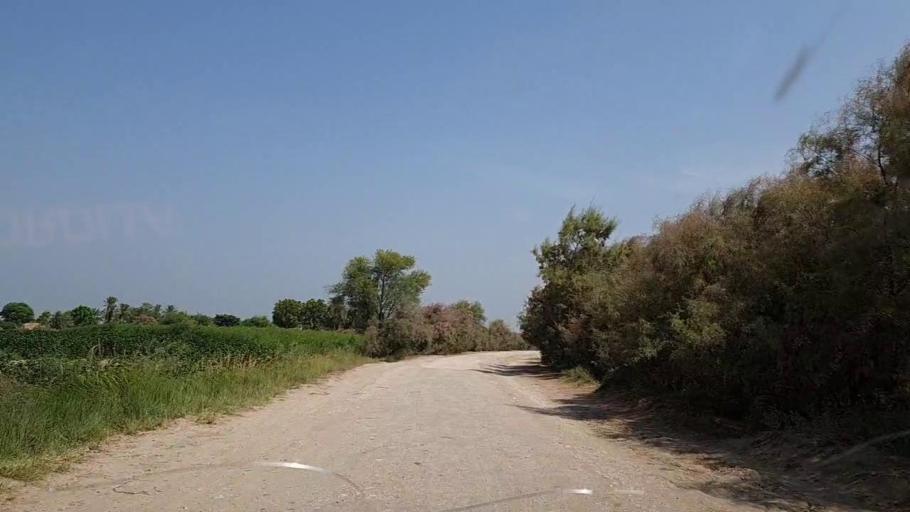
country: PK
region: Sindh
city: Adilpur
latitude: 27.8247
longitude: 69.3011
